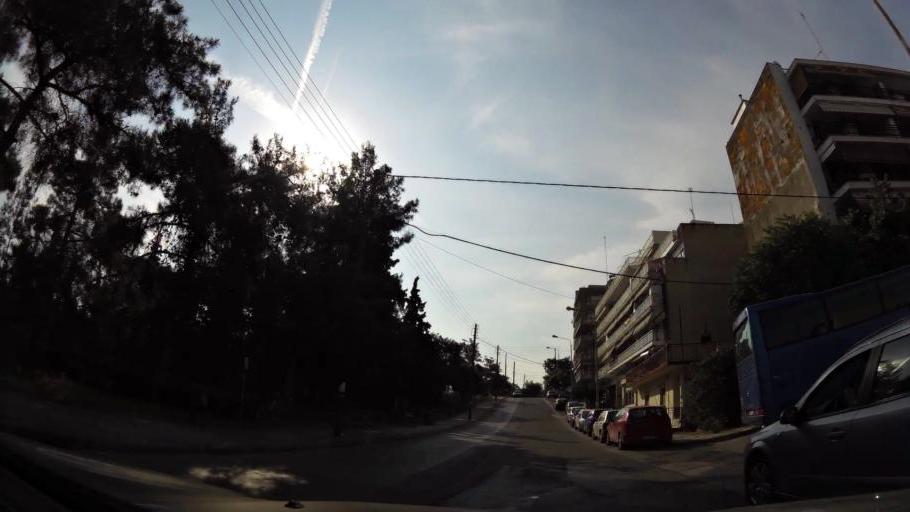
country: GR
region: Central Macedonia
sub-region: Nomos Thessalonikis
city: Polichni
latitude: 40.6586
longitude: 22.9485
